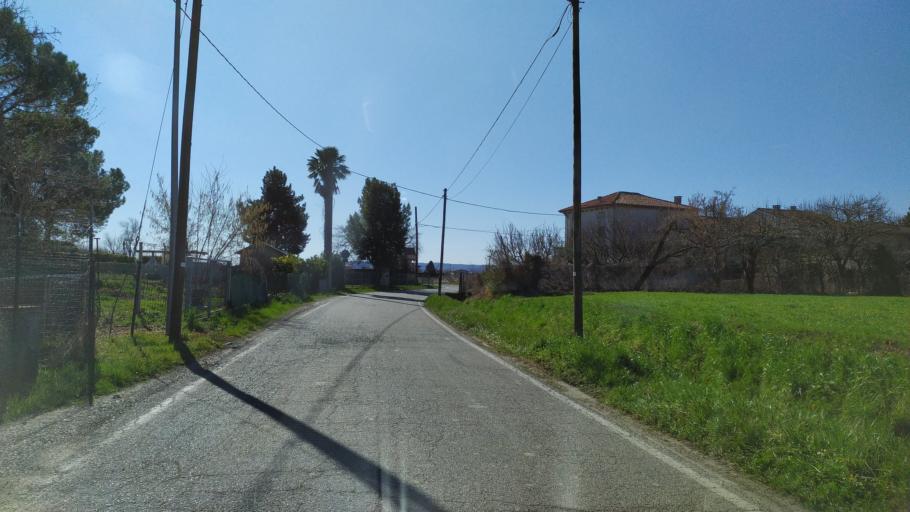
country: IT
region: Veneto
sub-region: Provincia di Vicenza
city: Vigardolo
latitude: 45.6117
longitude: 11.5973
